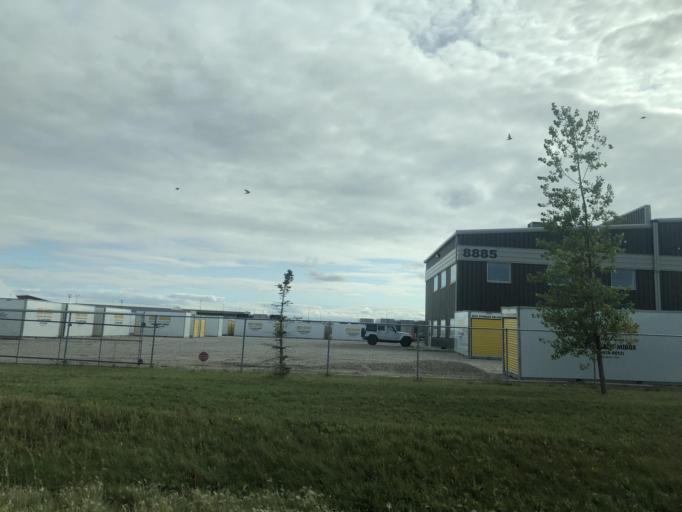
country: CA
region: Alberta
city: Chestermere
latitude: 50.9703
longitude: -113.9064
